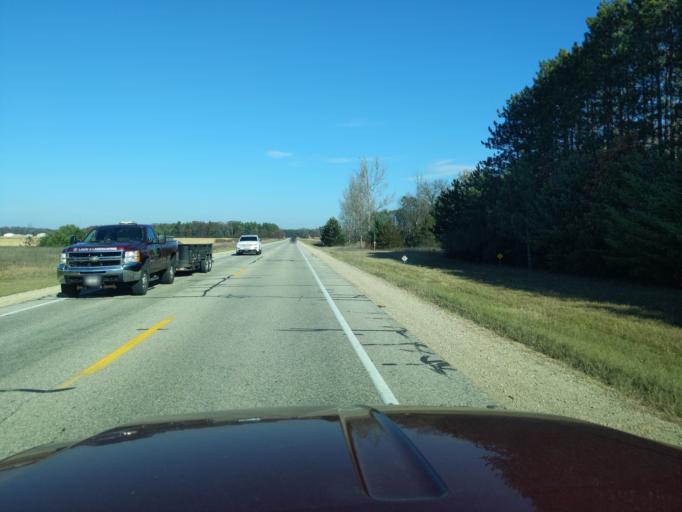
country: US
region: Wisconsin
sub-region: Waushara County
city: Wautoma
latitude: 44.0343
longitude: -89.2979
